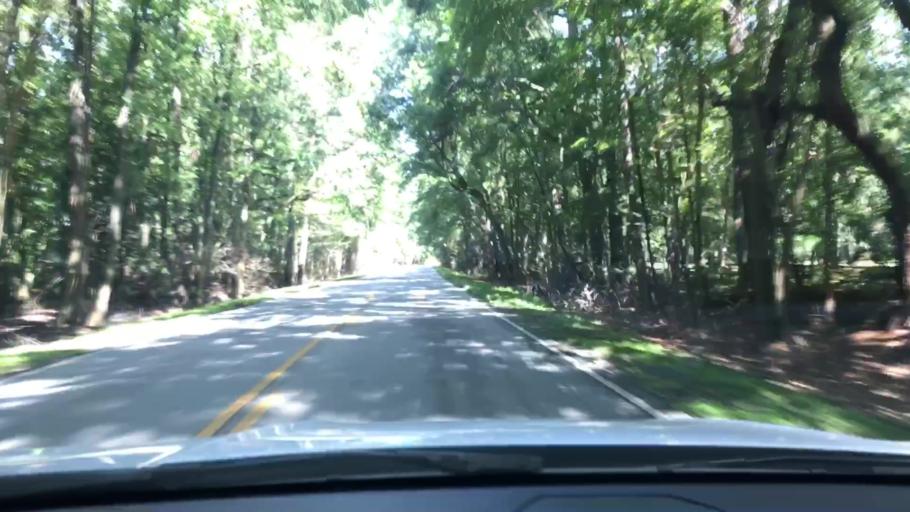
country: US
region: South Carolina
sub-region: Berkeley County
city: Ladson
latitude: 32.9006
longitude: -80.1419
